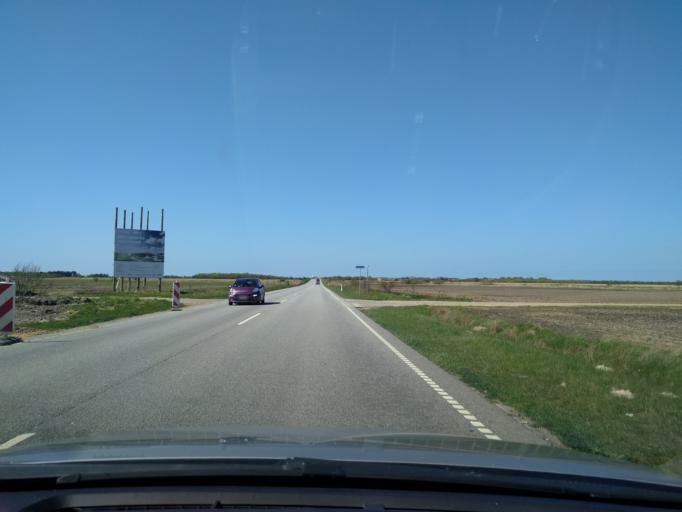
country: DK
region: Central Jutland
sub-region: Ringkobing-Skjern Kommune
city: Ringkobing
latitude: 56.1051
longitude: 8.2438
